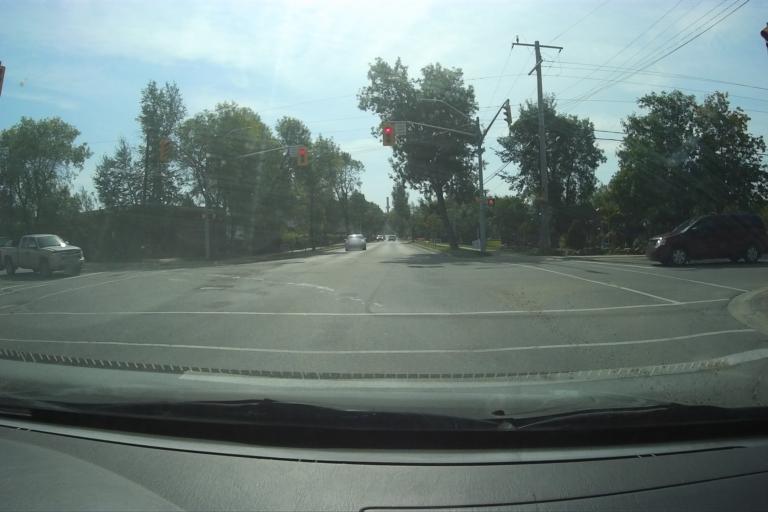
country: CA
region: Ontario
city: Kapuskasing
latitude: 49.4164
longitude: -82.4252
